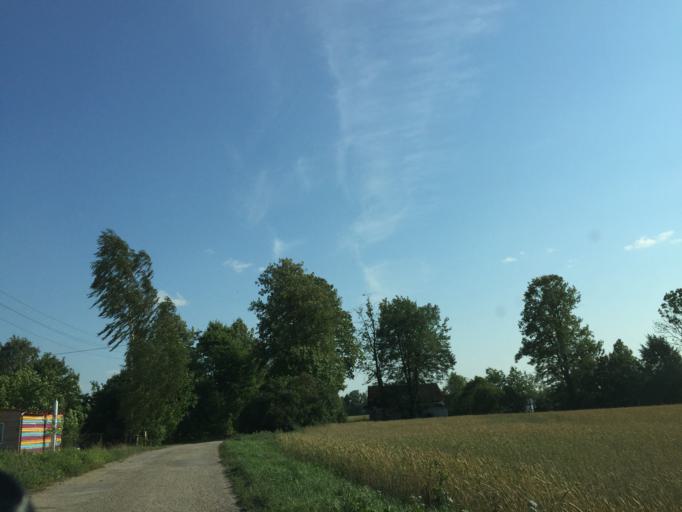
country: LV
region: Jelgava
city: Jelgava
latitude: 56.4548
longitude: 23.6810
